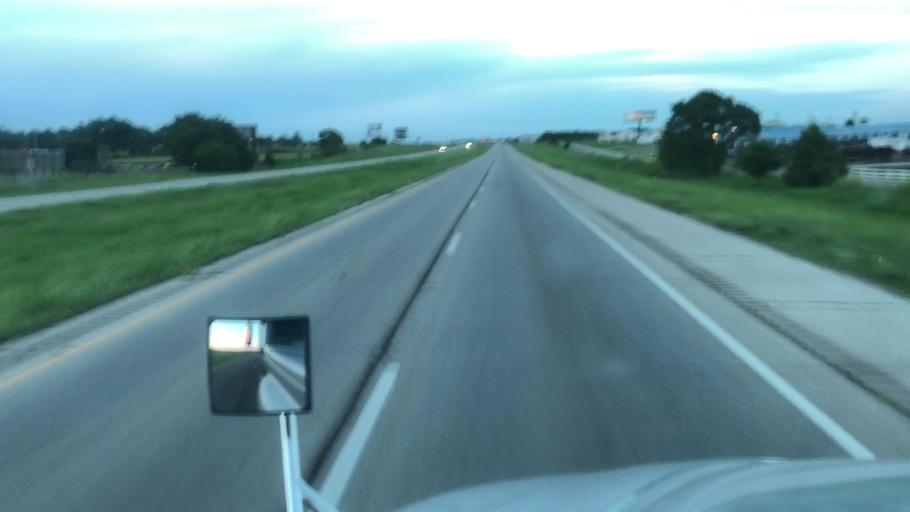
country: US
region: Oklahoma
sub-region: Kay County
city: Ponca City
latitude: 36.7552
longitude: -97.0653
